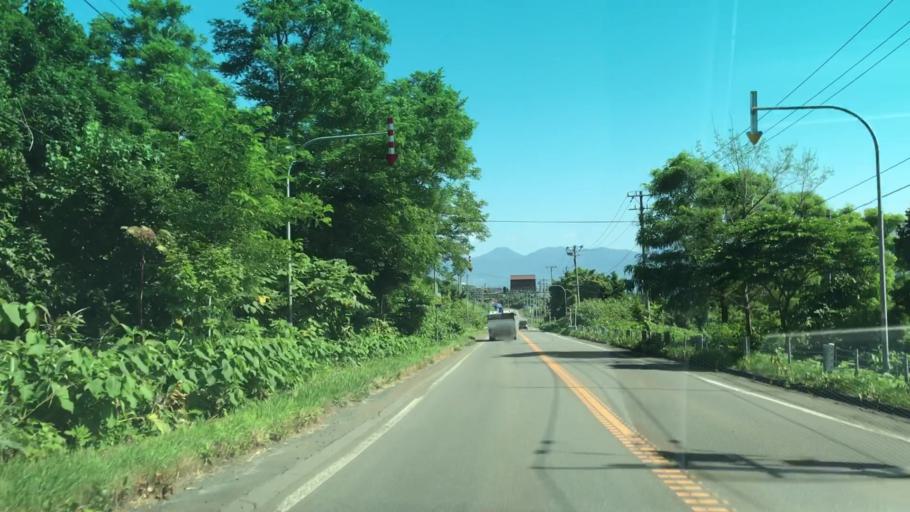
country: JP
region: Hokkaido
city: Iwanai
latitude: 43.0762
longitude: 140.4872
